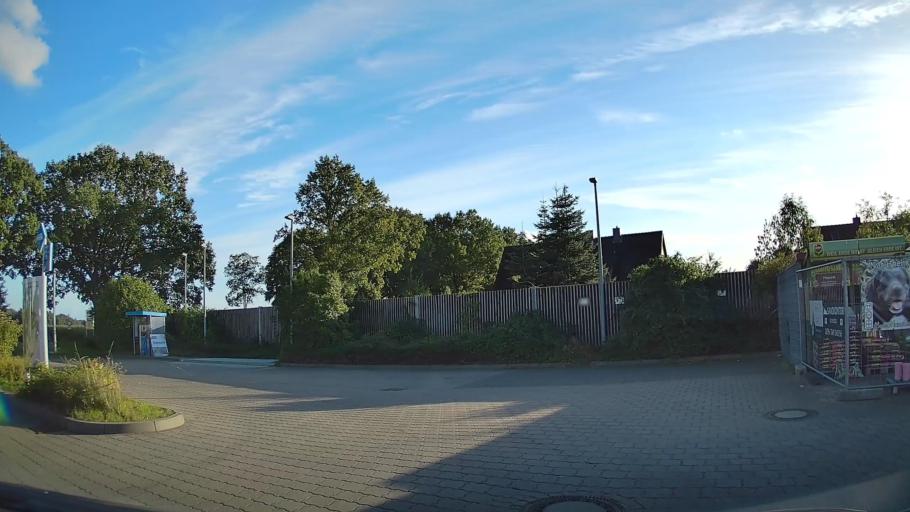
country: DE
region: Lower Saxony
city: Scheessel
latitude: 53.1755
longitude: 9.4928
